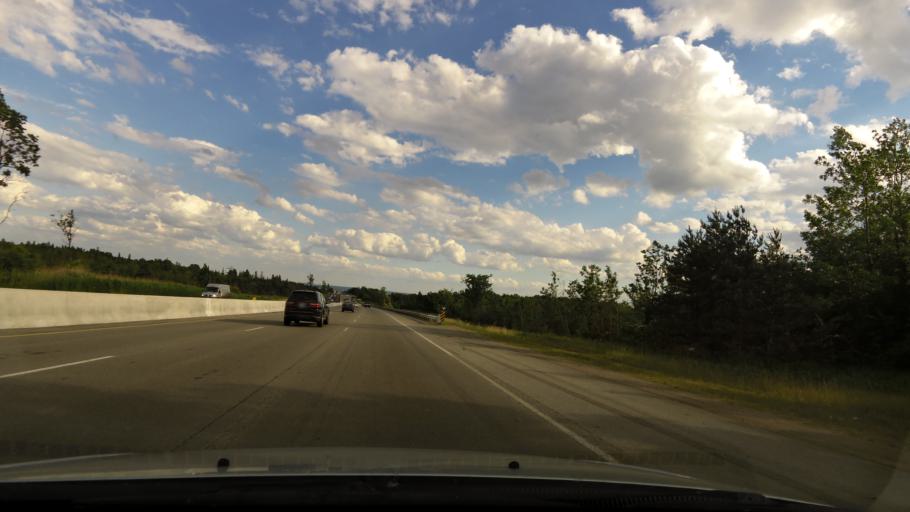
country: CA
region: Ontario
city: Bradford West Gwillimbury
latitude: 44.1459
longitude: -79.6422
